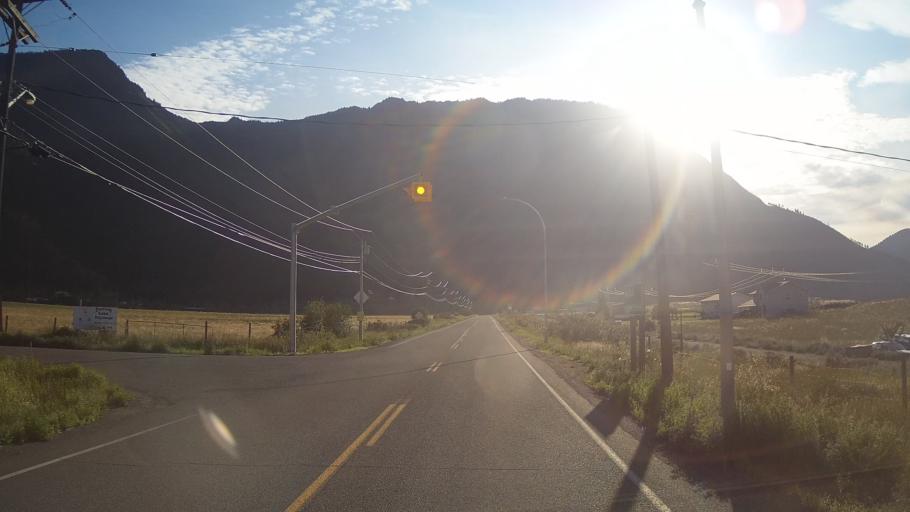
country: CA
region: British Columbia
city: Lillooet
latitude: 50.7424
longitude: -121.8639
